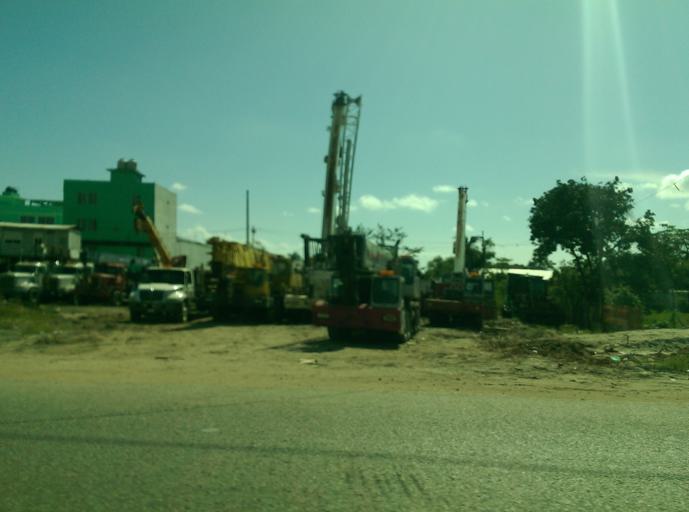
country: MX
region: Tabasco
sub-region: Centro
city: Anacleto Canabal 2da. Seccion
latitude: 17.9824
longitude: -93.0202
